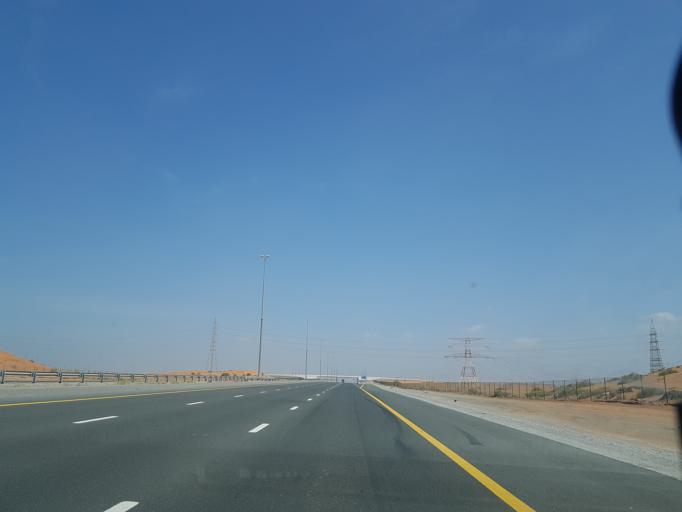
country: AE
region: Ra's al Khaymah
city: Ras al-Khaimah
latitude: 25.6897
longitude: 55.9183
